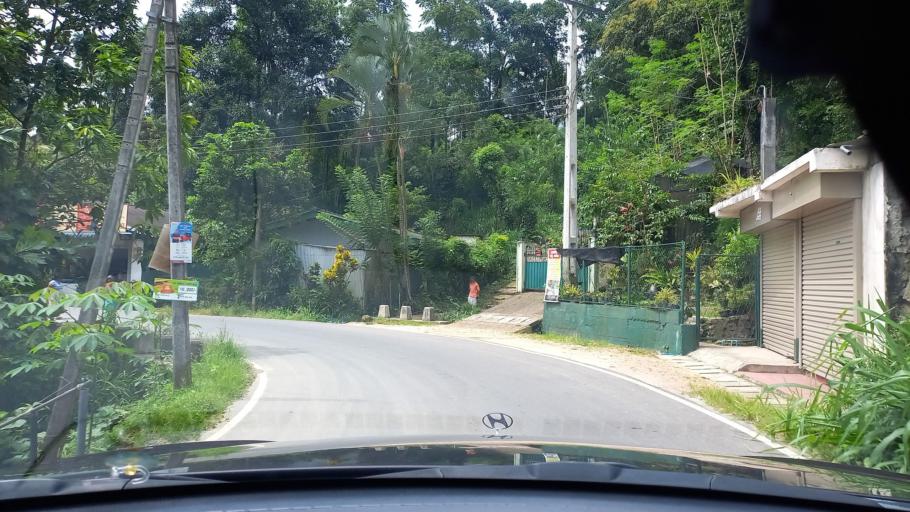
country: LK
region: Central
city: Gampola
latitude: 7.2185
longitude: 80.6142
